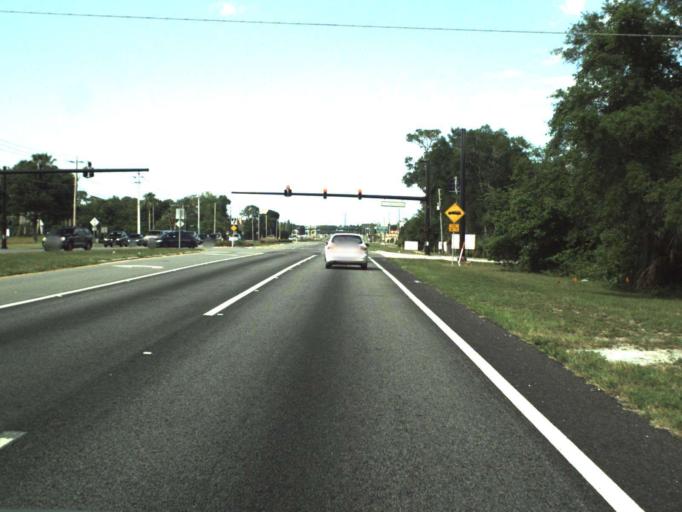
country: US
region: Florida
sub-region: Seminole County
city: Lake Mary
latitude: 28.7415
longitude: -81.2992
